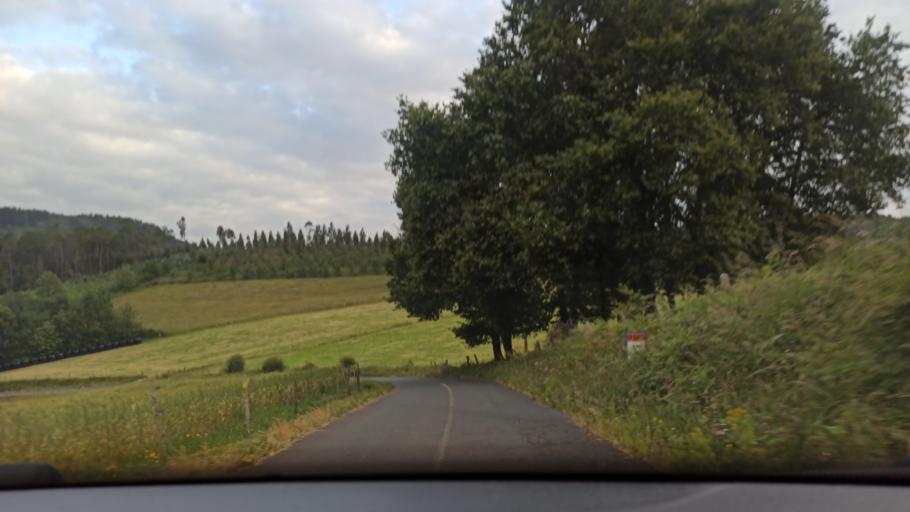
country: ES
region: Galicia
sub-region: Provincia da Coruna
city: Santiso
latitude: 42.8193
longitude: -8.1424
